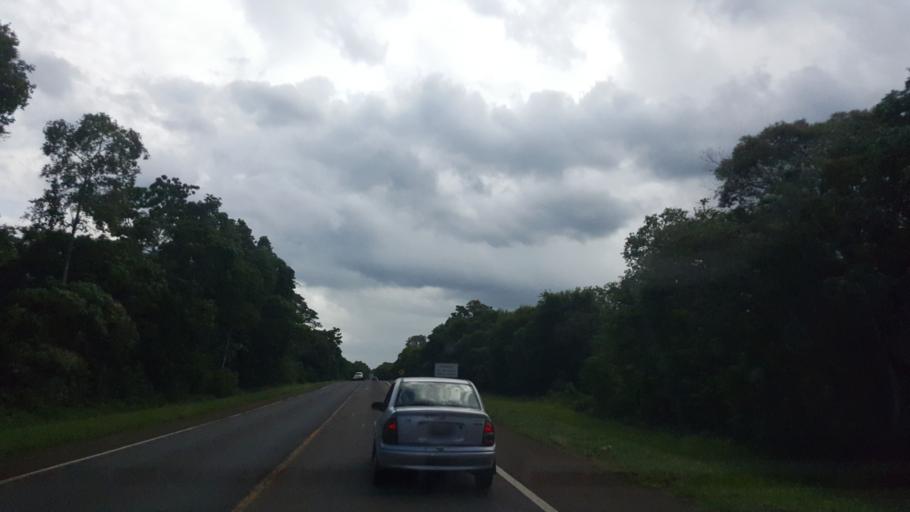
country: AR
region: Misiones
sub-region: Departamento de Iguazu
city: Puerto Iguazu
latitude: -25.7192
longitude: -54.5219
